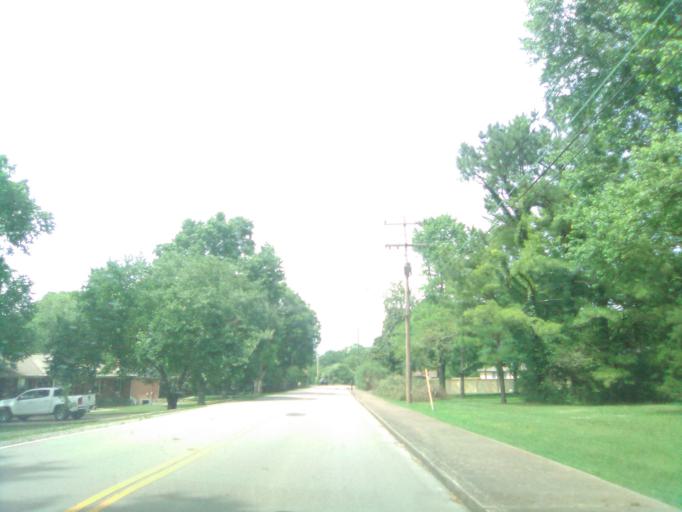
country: US
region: Tennessee
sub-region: Davidson County
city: Belle Meade
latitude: 36.1225
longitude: -86.9019
